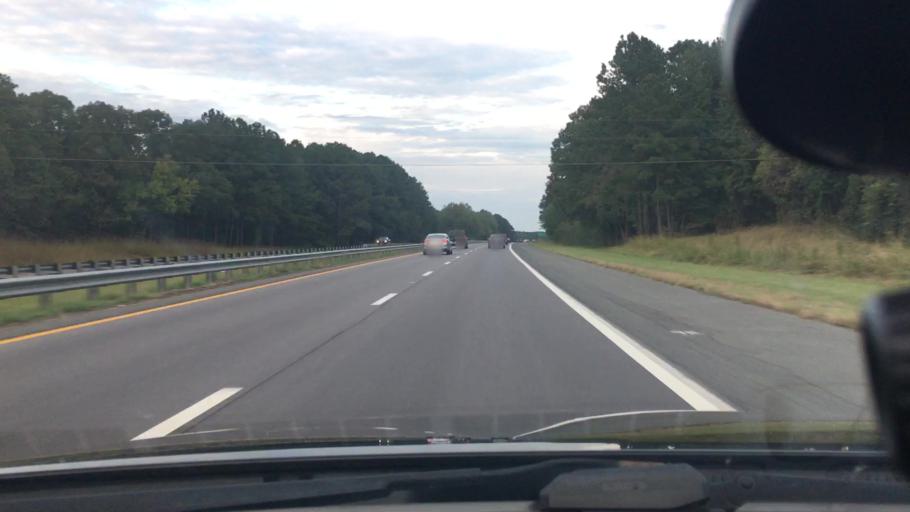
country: US
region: North Carolina
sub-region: Chatham County
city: Farmville
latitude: 35.6080
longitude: -79.1060
